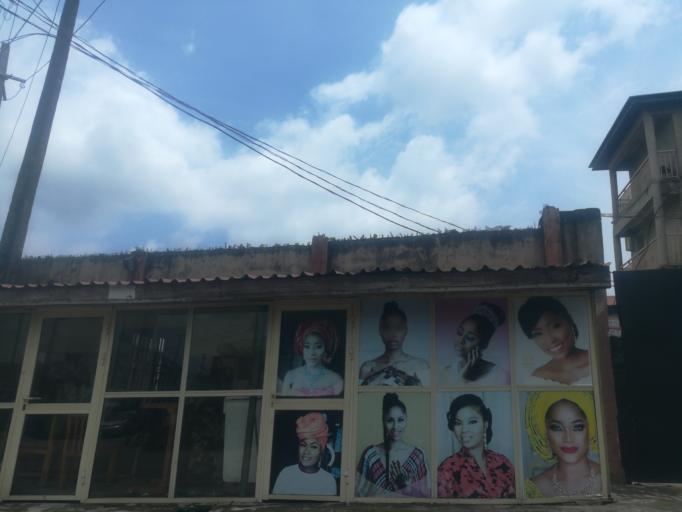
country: NG
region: Lagos
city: Ojota
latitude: 6.5640
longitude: 3.3951
